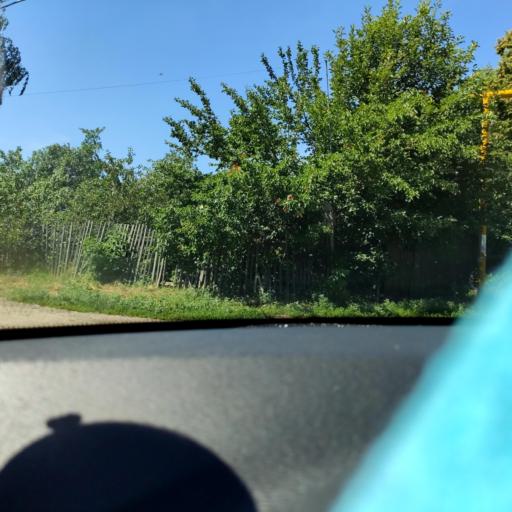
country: RU
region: Samara
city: Smyshlyayevka
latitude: 53.2441
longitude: 50.3517
